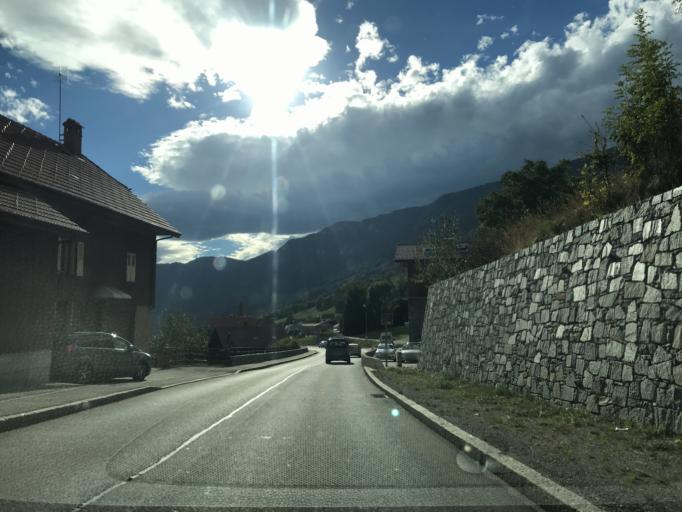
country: FR
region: Rhone-Alpes
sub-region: Departement de la Haute-Savoie
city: Saint-Jean-de-Sixt
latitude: 45.9100
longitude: 6.3698
